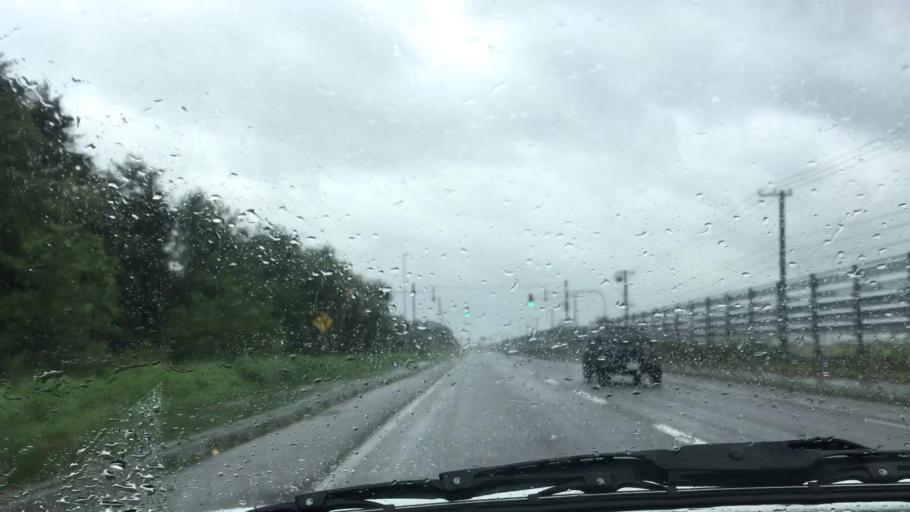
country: JP
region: Hokkaido
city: Nanae
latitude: 42.3089
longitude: 140.2728
